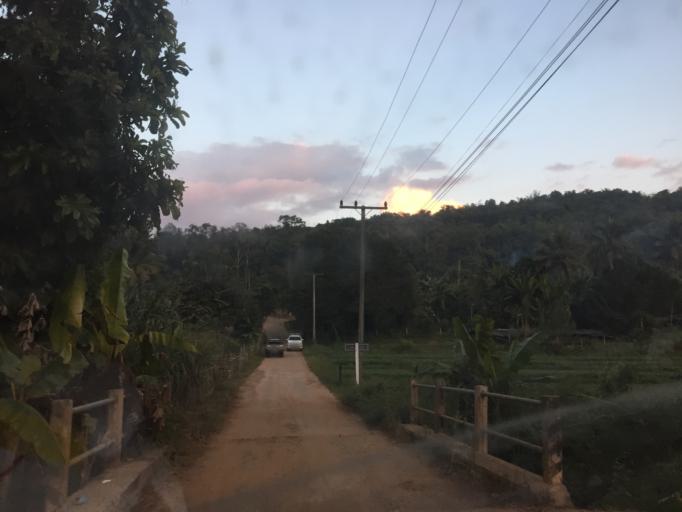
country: TH
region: Chiang Mai
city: Samoeng
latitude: 19.0067
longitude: 98.7083
